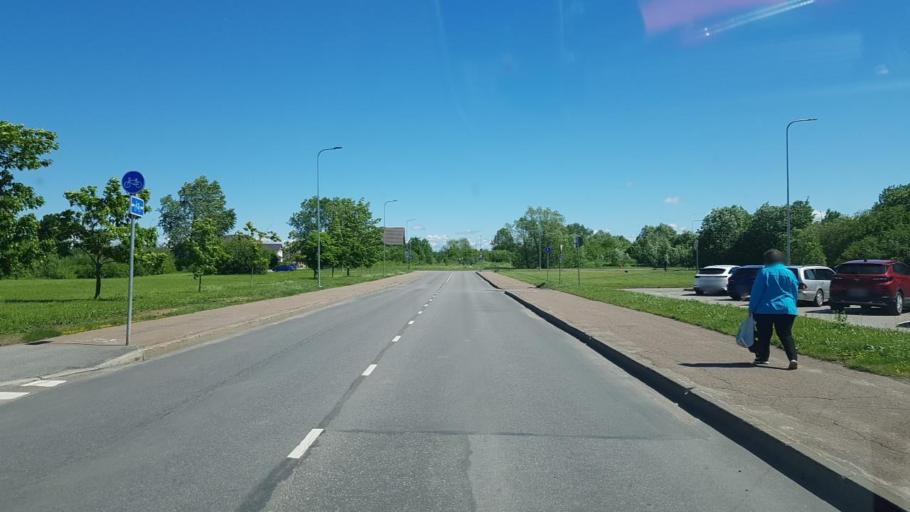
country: EE
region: Ida-Virumaa
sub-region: Narva linn
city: Narva
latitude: 59.3889
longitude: 28.1839
